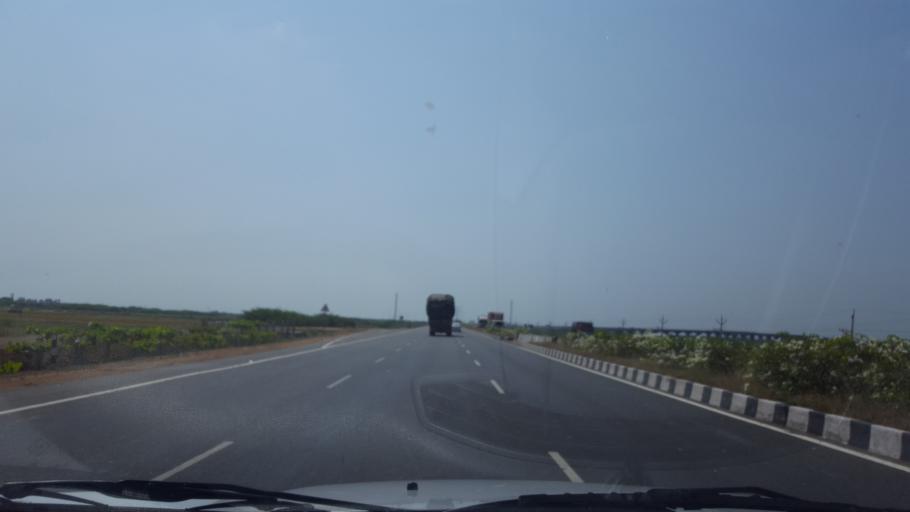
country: IN
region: Andhra Pradesh
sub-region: Prakasam
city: Ongole
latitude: 15.4809
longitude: 80.0611
